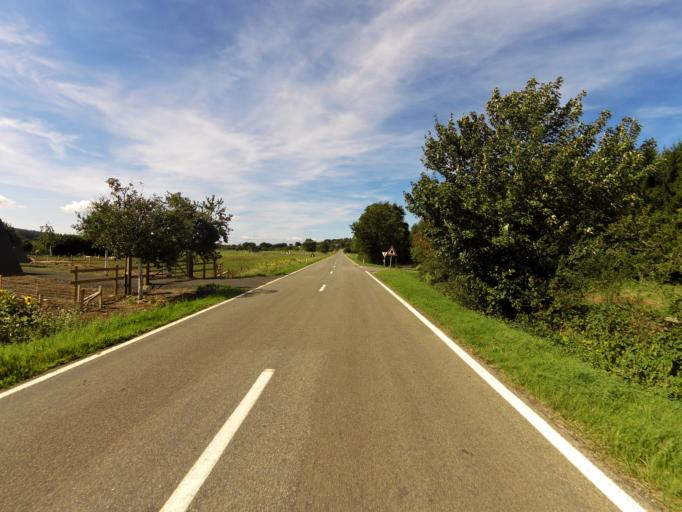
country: BE
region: Wallonia
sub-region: Province du Luxembourg
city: Nassogne
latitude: 50.1273
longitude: 5.3628
